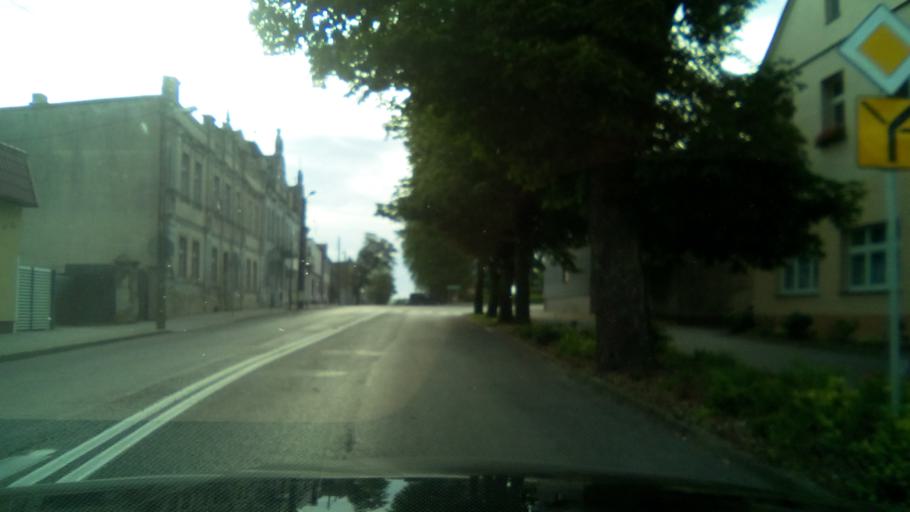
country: PL
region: Greater Poland Voivodeship
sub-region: Powiat gnieznienski
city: Witkowo
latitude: 52.4414
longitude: 17.7697
